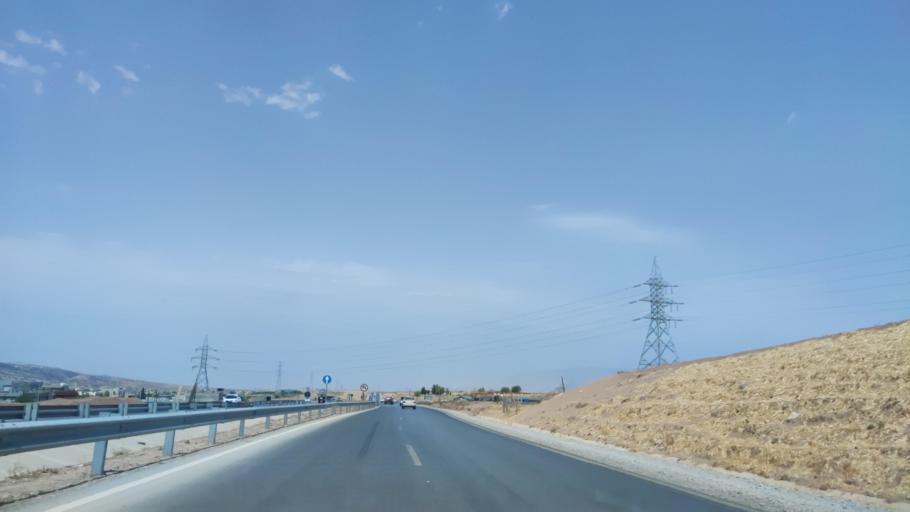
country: IQ
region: Arbil
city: Shaqlawah
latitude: 36.5044
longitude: 44.3530
